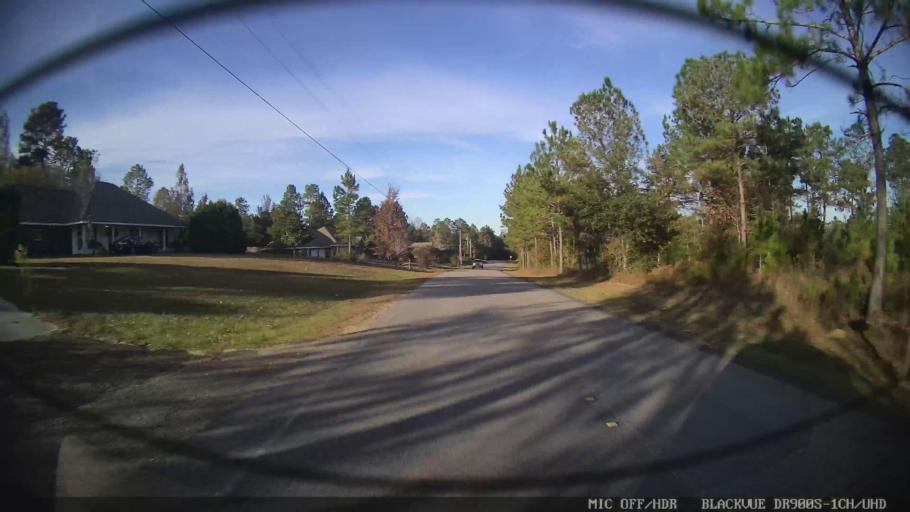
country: US
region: Mississippi
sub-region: Lamar County
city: Purvis
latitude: 31.1448
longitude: -89.3413
